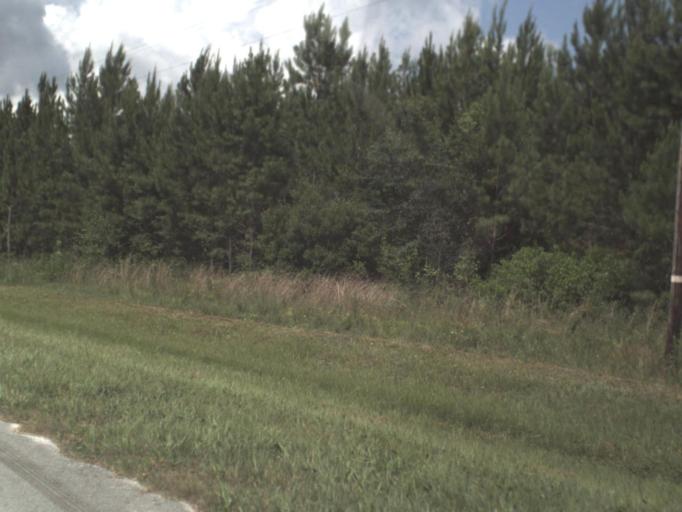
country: US
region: Florida
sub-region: Baker County
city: Macclenny
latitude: 30.2182
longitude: -82.1515
